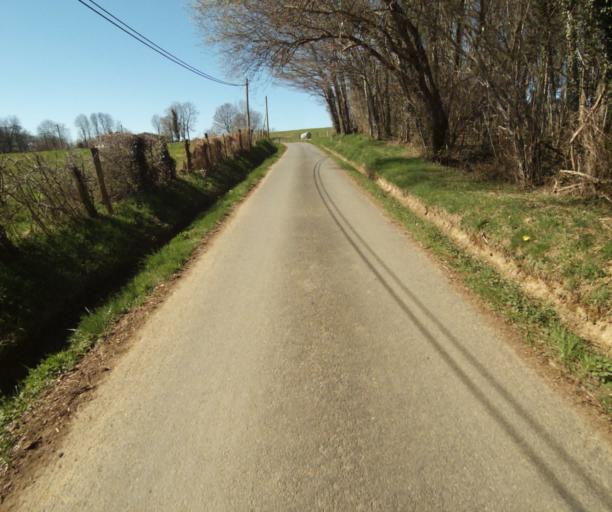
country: FR
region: Limousin
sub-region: Departement de la Correze
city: Chamboulive
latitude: 45.3954
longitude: 1.6657
